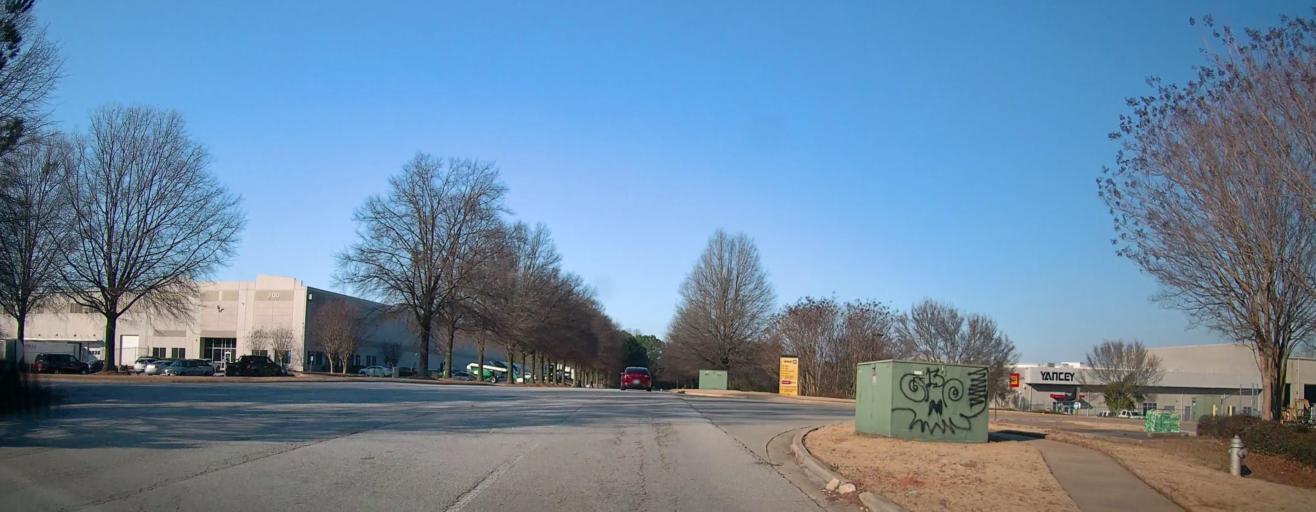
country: US
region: Georgia
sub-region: Henry County
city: McDonough
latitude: 33.4074
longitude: -84.1708
